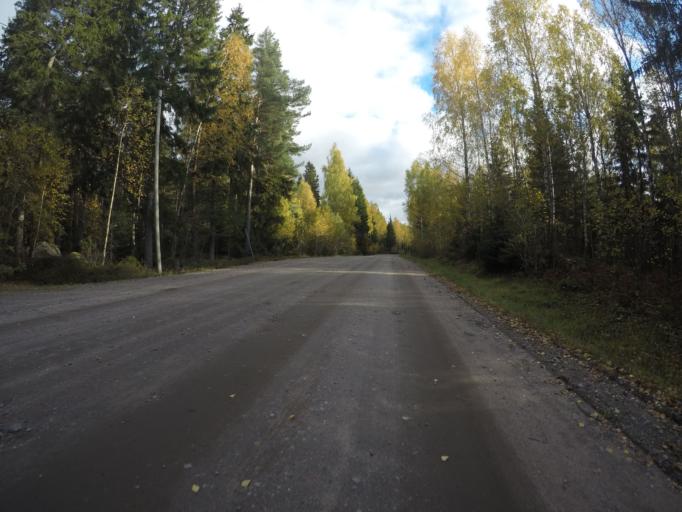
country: SE
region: Vaestmanland
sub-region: Arboga Kommun
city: Tyringe
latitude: 59.3731
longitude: 15.9511
